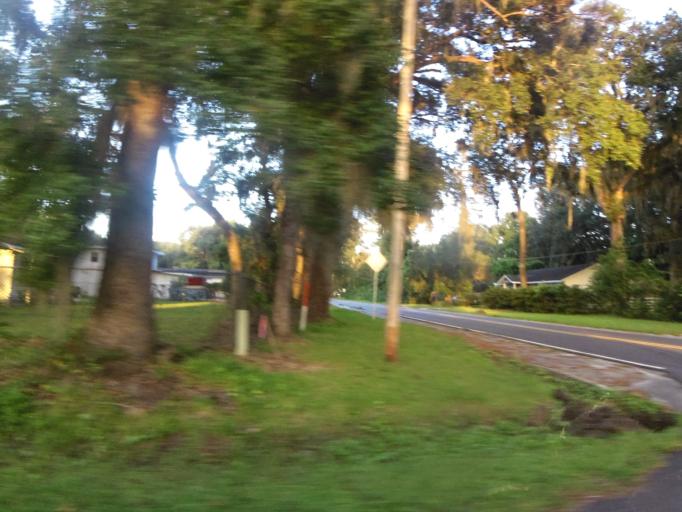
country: US
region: Georgia
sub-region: Camden County
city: Kingsland
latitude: 30.7983
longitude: -81.6936
